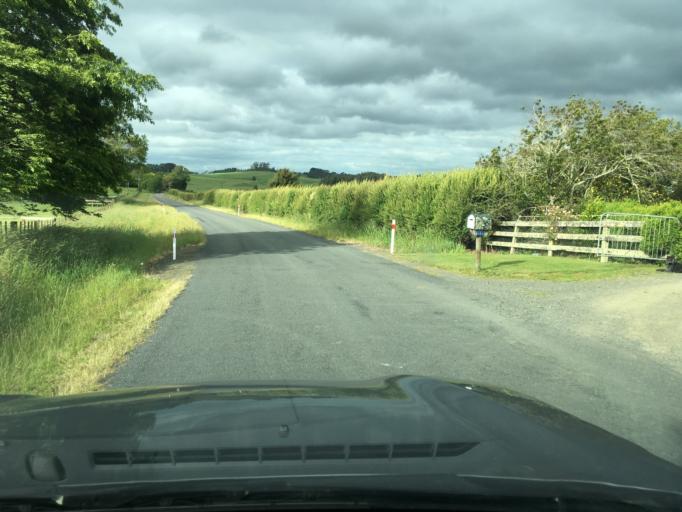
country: NZ
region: Waikato
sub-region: Hamilton City
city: Hamilton
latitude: -37.8212
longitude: 175.1774
